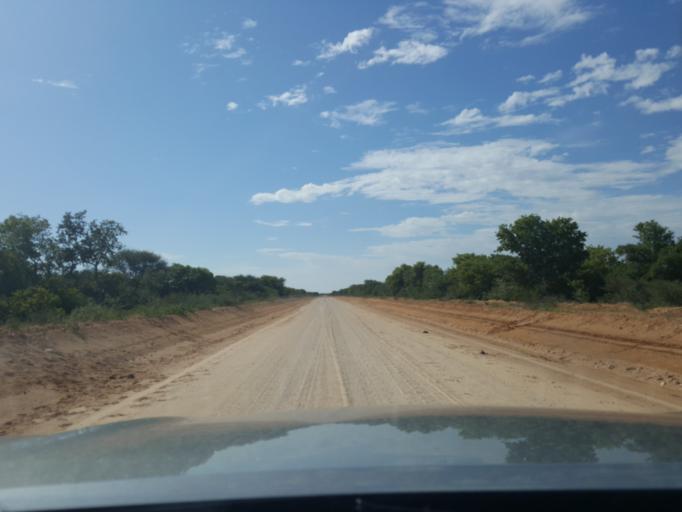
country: BW
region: Kweneng
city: Khudumelapye
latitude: -23.7545
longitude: 24.7570
